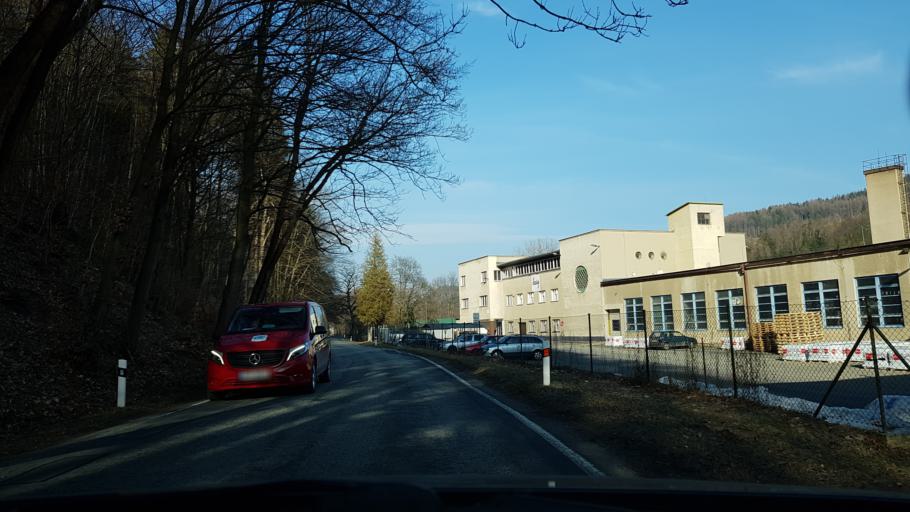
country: CZ
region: Olomoucky
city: Dolni Bohdikov
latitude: 50.0238
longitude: 16.8963
